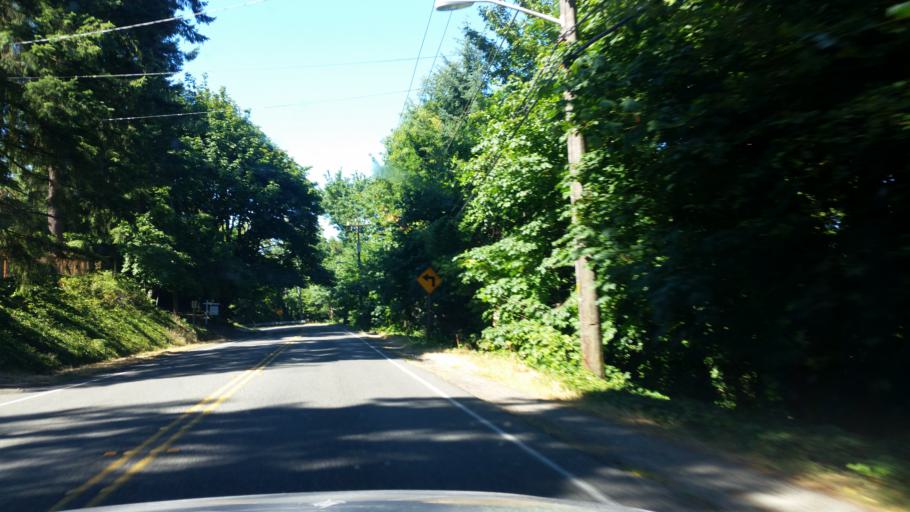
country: US
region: Washington
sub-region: King County
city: Lake Forest Park
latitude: 47.7563
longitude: -122.3022
